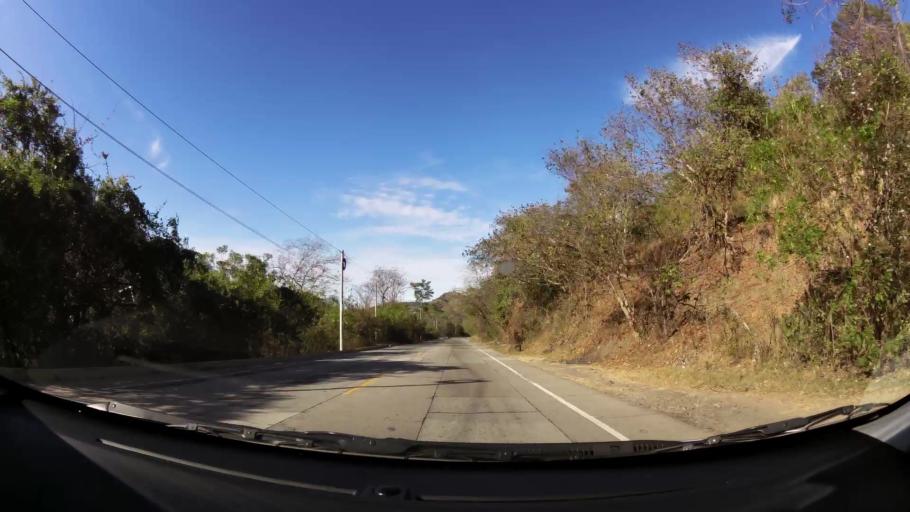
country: SV
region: Santa Ana
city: Texistepeque
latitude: 14.1514
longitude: -89.5141
